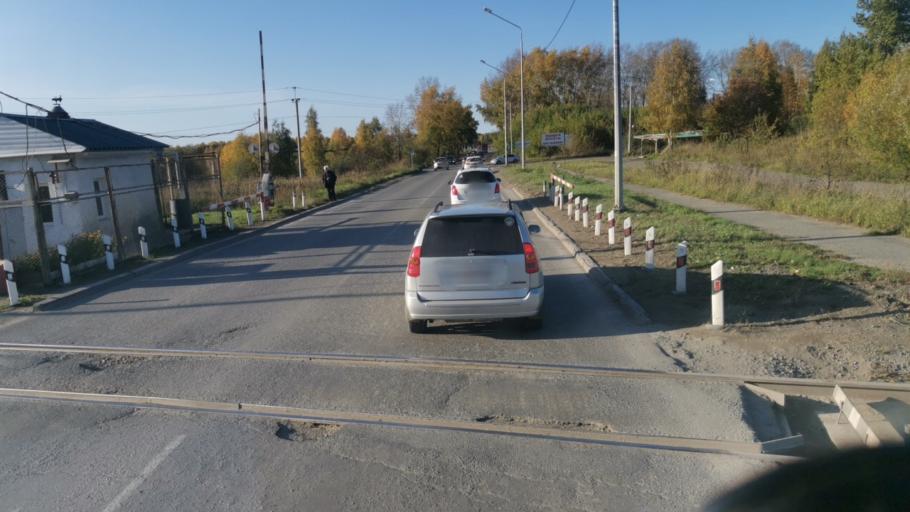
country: RU
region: Sverdlovsk
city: Nizhniy Tagil
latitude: 57.9430
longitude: 59.9220
